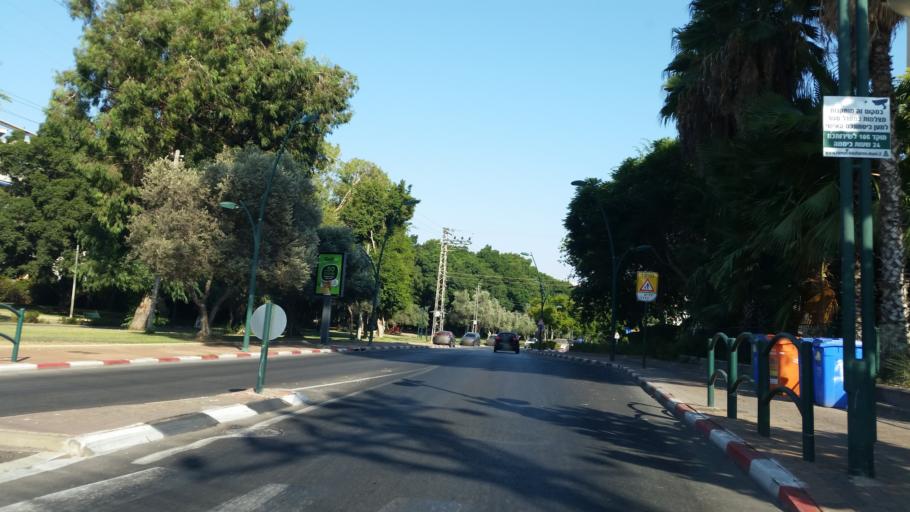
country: IL
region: Tel Aviv
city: Ramat HaSharon
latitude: 32.1306
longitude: 34.8530
